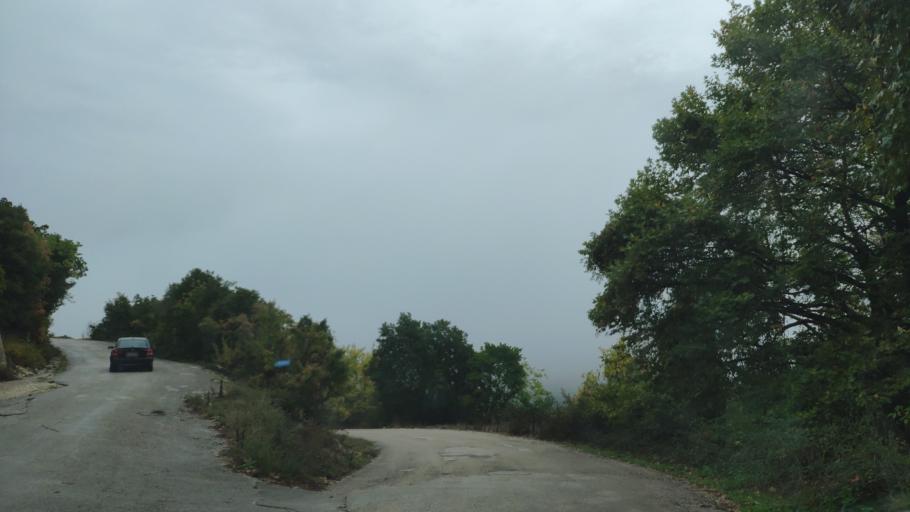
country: GR
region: Epirus
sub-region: Nomos Thesprotias
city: Paramythia
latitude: 39.4724
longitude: 20.6685
